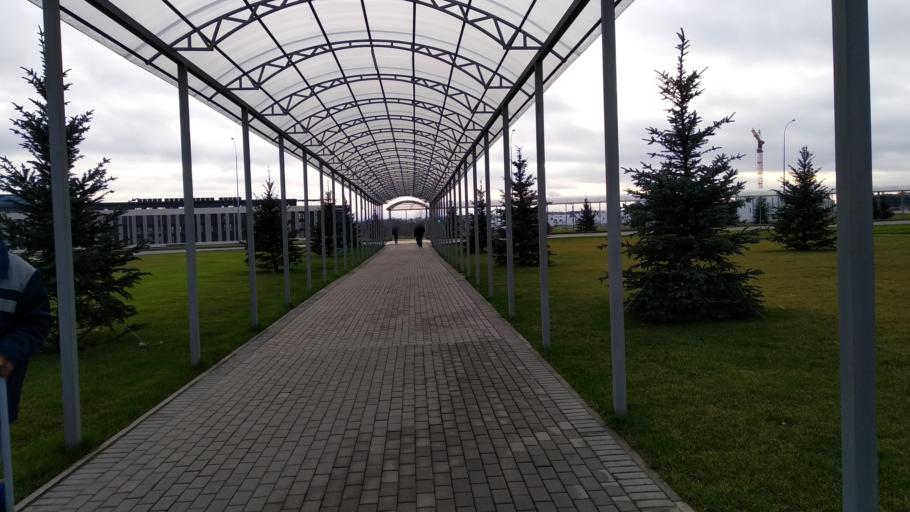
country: RU
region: Moskovskaya
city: Novoivanovskoye
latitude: 55.6983
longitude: 37.3465
